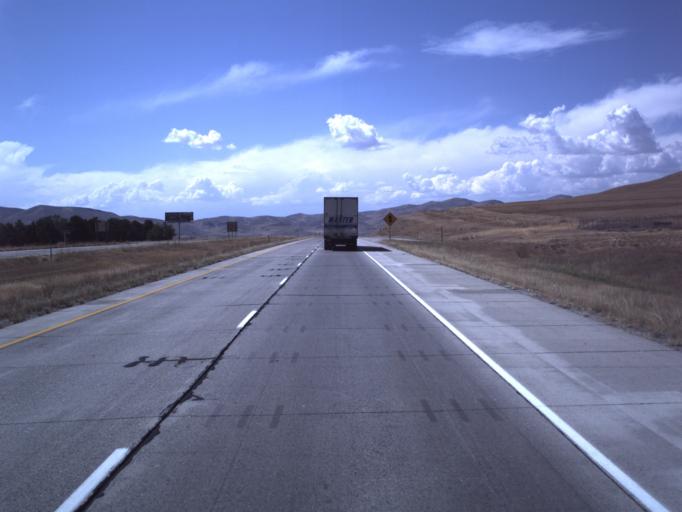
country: US
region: Utah
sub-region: Box Elder County
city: Tremonton
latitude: 41.7214
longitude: -112.2301
